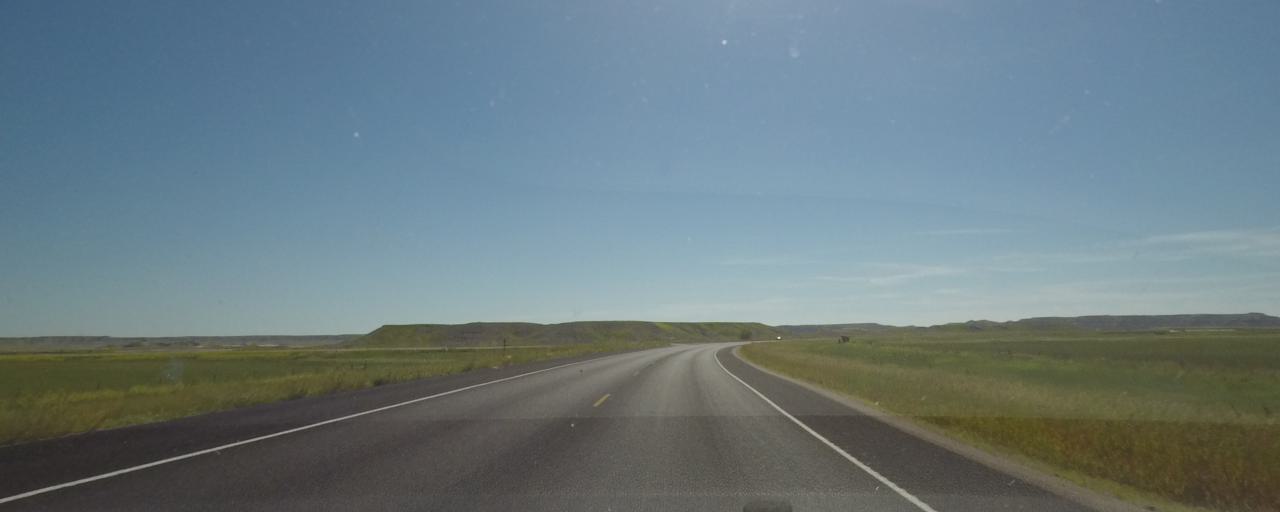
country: US
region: South Dakota
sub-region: Shannon County
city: Porcupine
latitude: 43.7780
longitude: -102.5392
